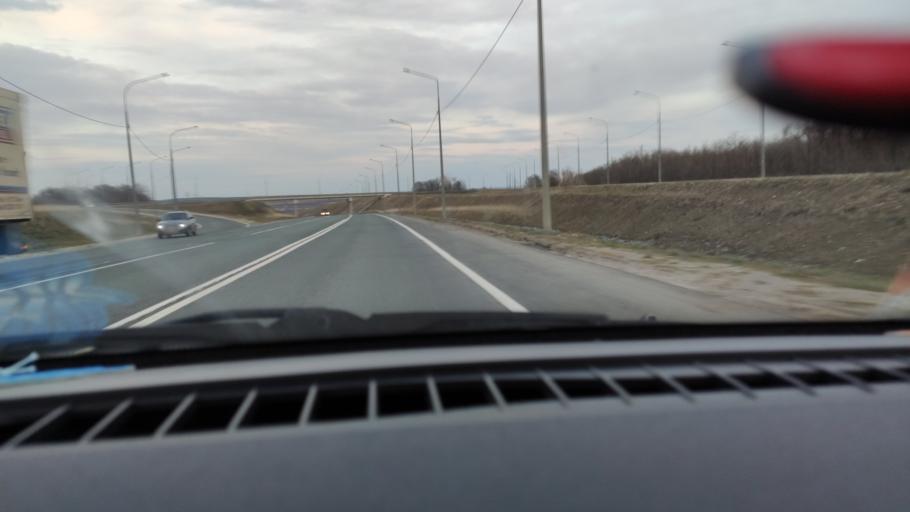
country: RU
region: Saratov
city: Yelshanka
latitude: 51.8202
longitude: 46.3663
